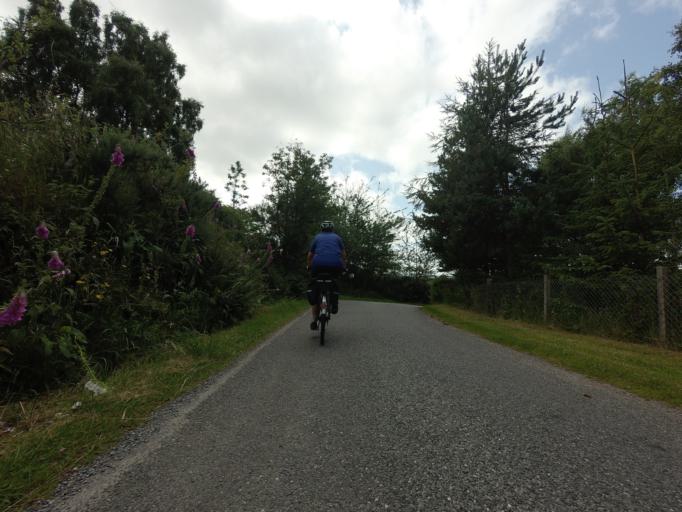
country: GB
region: Scotland
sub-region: Highland
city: Fortrose
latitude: 57.4740
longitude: -4.0649
